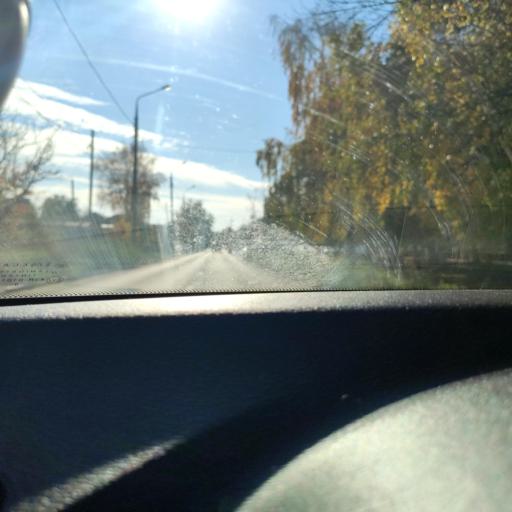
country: RU
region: Samara
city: Petra-Dubrava
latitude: 53.2334
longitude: 50.2991
